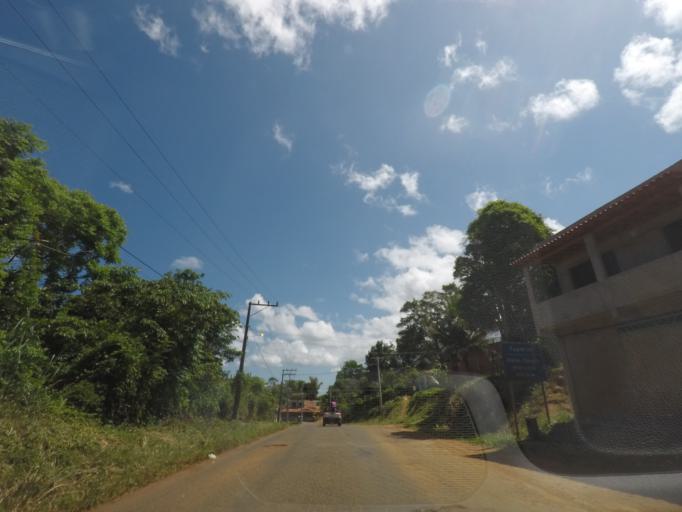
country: BR
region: Bahia
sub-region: Taperoa
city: Taperoa
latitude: -13.5298
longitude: -39.1043
